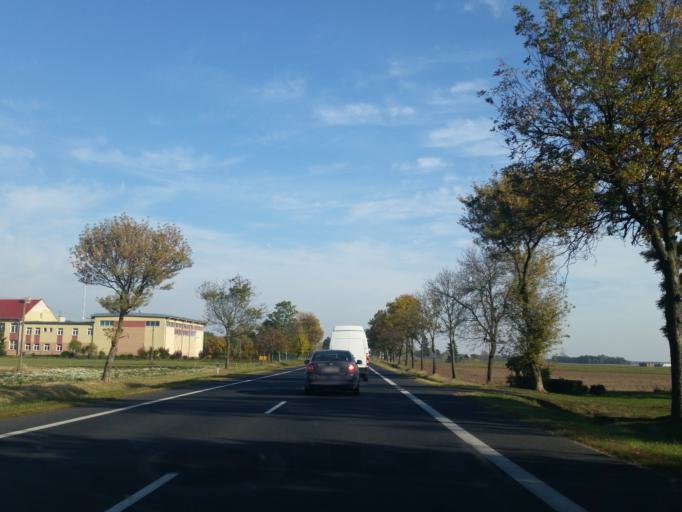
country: PL
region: Masovian Voivodeship
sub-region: Powiat sierpecki
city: Zawidz
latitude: 52.8090
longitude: 19.8279
